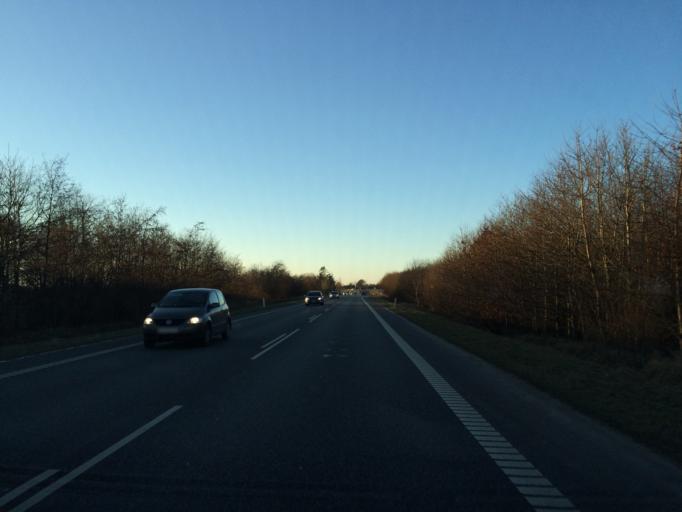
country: DK
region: Central Jutland
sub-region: Randers Kommune
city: Langa
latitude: 56.4769
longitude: 9.9155
